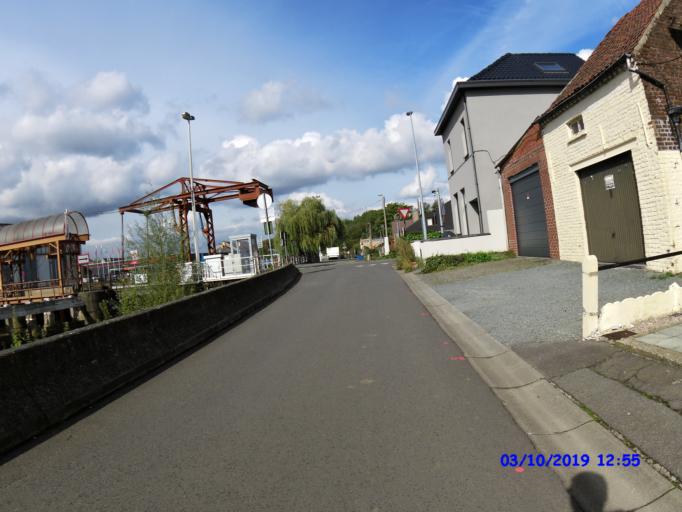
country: BE
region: Flanders
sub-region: Provincie Oost-Vlaanderen
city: Denderleeuw
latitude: 50.8918
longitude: 4.0822
